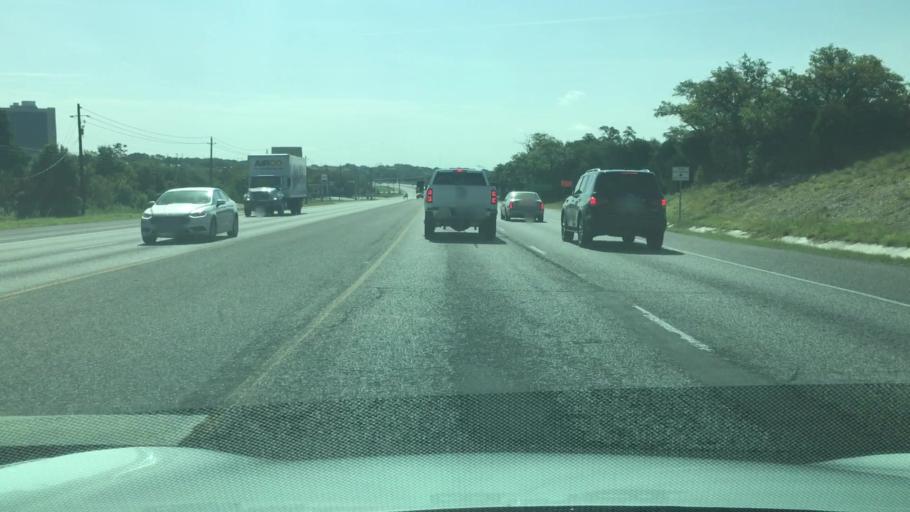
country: US
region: Texas
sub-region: Travis County
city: Barton Creek
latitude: 30.2314
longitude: -97.8905
